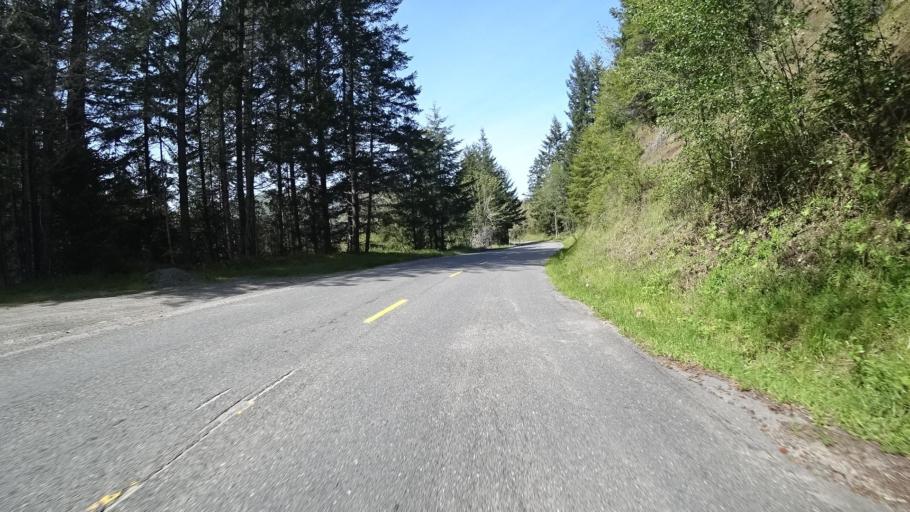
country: US
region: California
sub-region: Humboldt County
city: Rio Dell
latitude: 40.4584
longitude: -123.8043
